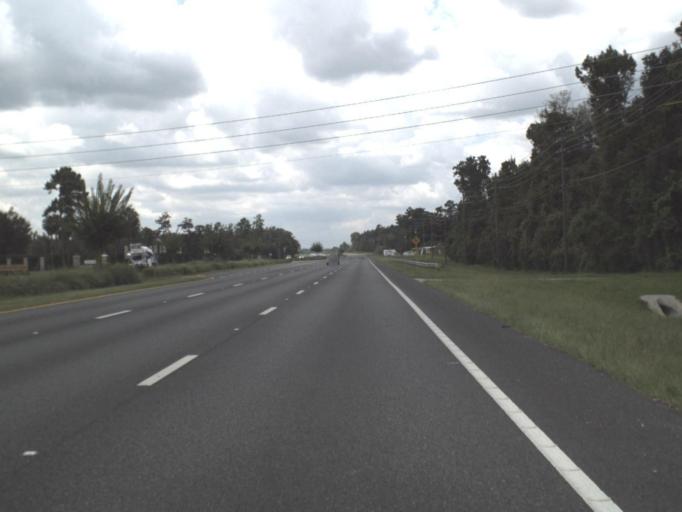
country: US
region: Florida
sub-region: Hernando County
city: South Brooksville
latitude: 28.5157
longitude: -82.4174
